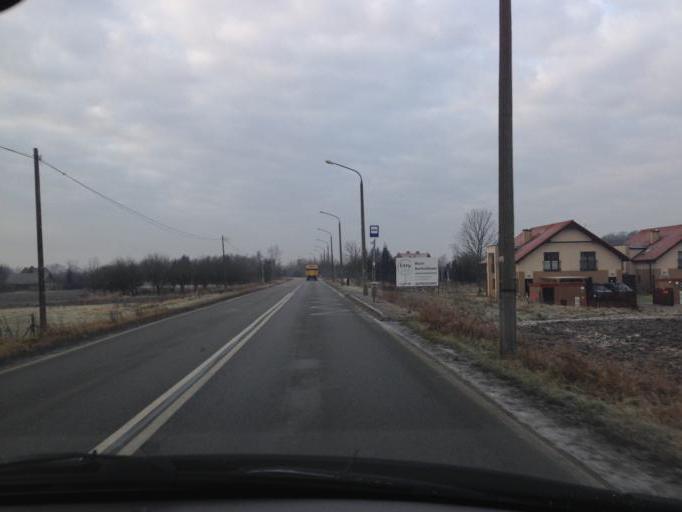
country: PL
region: Lesser Poland Voivodeship
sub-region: Powiat wielicki
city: Kokotow
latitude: 50.0561
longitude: 20.0664
